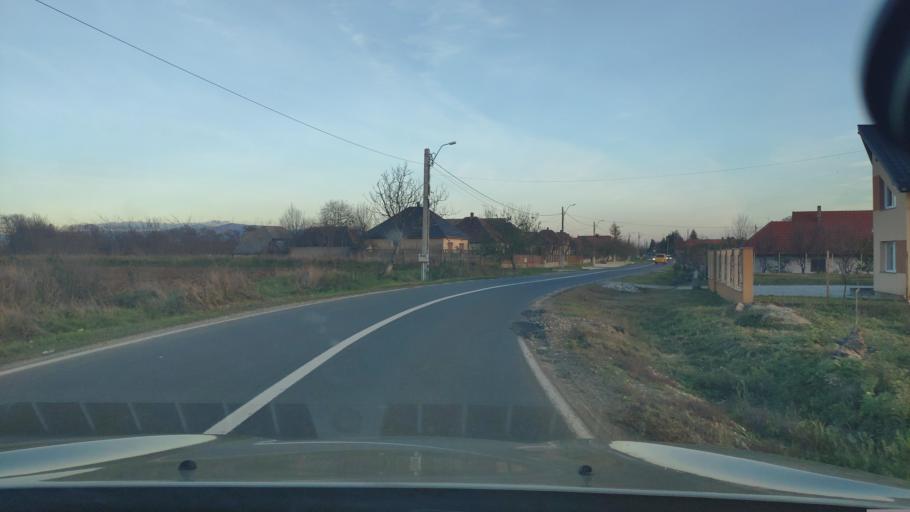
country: RO
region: Satu Mare
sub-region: Comuna Apa
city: Apa
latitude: 47.7665
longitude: 23.1814
